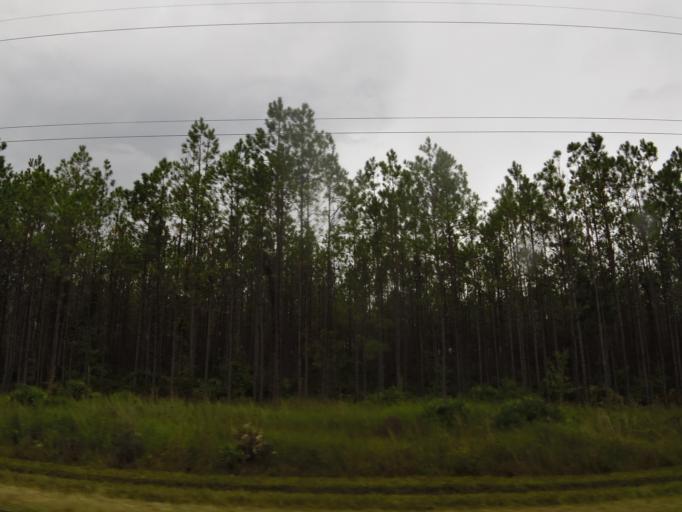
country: US
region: Florida
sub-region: Duval County
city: Baldwin
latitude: 30.4709
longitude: -82.0546
